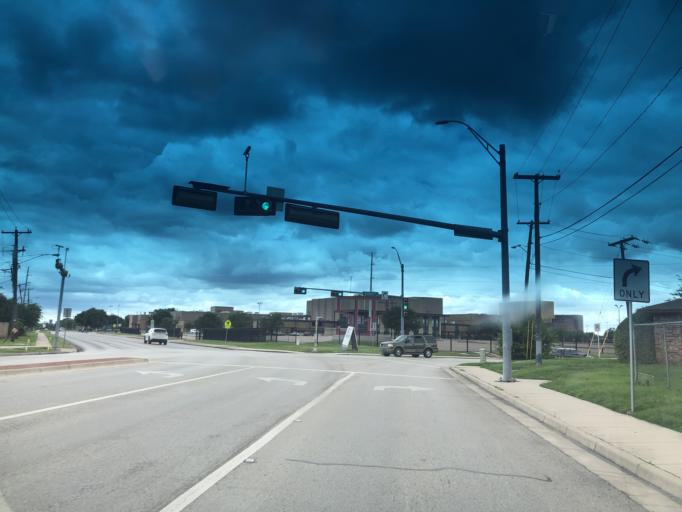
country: US
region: Texas
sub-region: Dallas County
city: Grand Prairie
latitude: 32.6984
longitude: -97.0030
